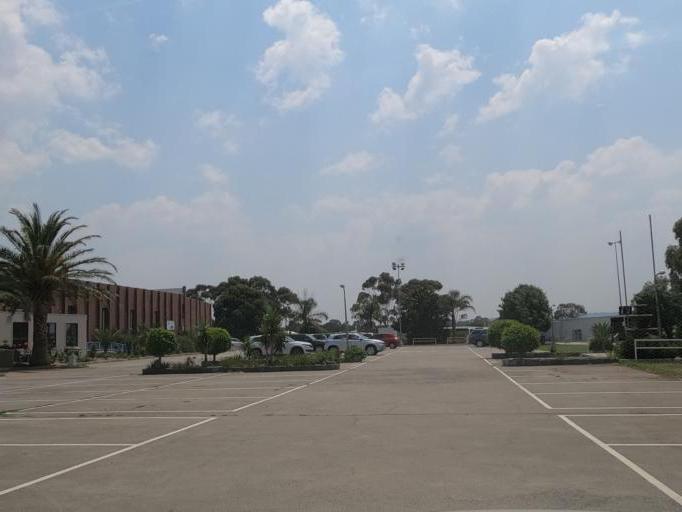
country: AU
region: Victoria
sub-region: Hume
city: Greenvale
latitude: -37.6397
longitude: 144.8247
